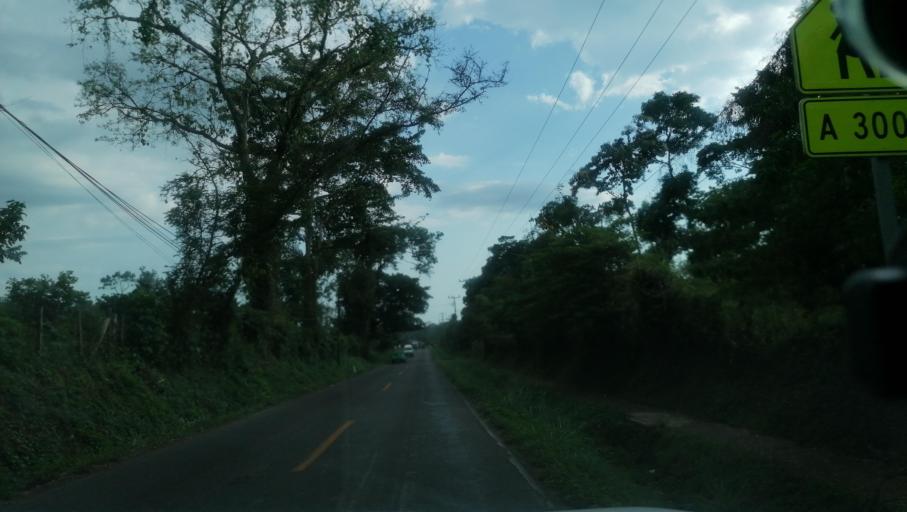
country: MX
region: Chiapas
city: Cacahoatan
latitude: 15.0108
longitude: -92.1556
